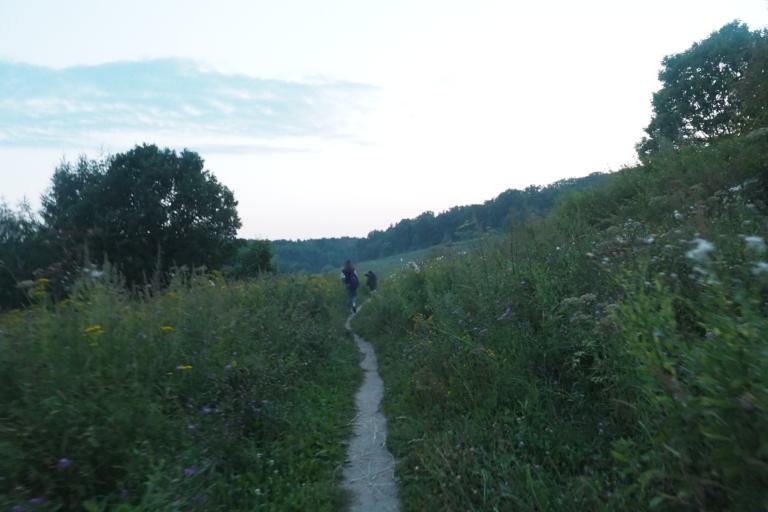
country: RU
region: Moscow
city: Orekhovo-Borisovo Severnoye
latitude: 55.6083
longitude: 37.6925
